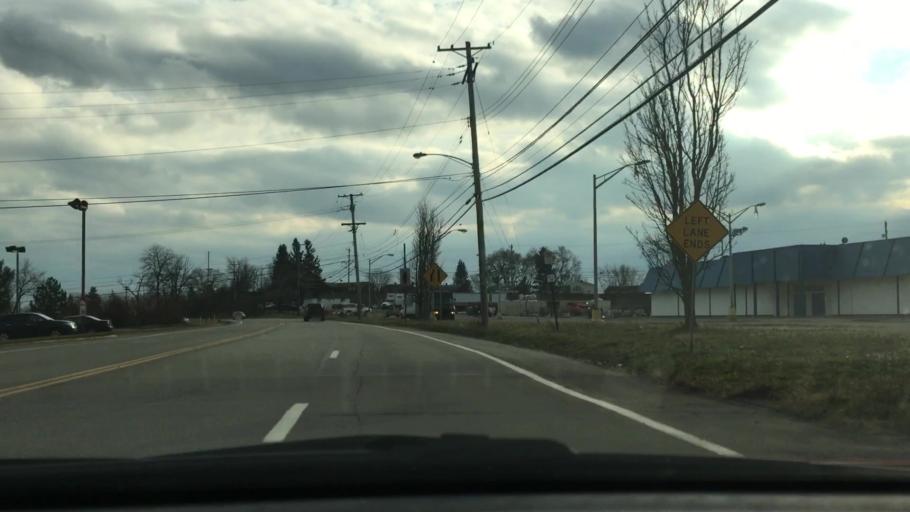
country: US
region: Pennsylvania
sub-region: Allegheny County
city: Pleasant Hills
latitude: 40.3492
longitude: -79.9271
